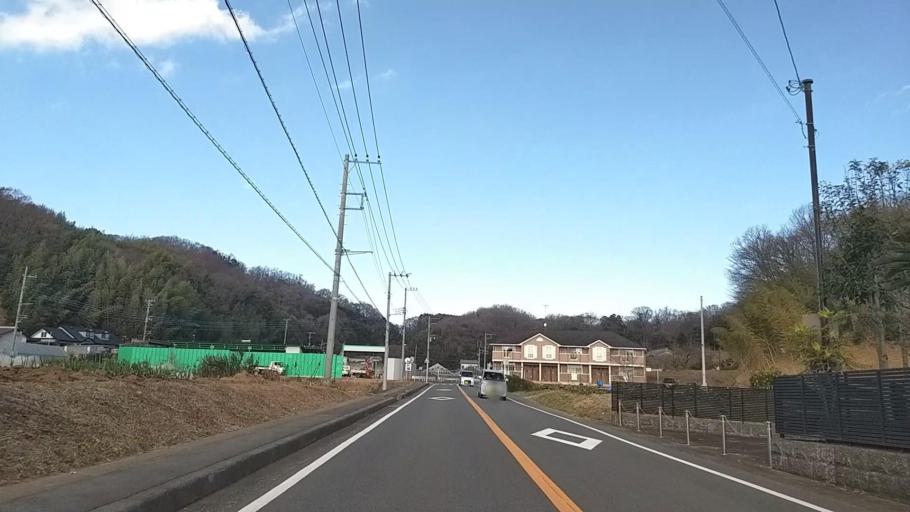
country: JP
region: Kanagawa
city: Isehara
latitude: 35.4181
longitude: 139.3125
